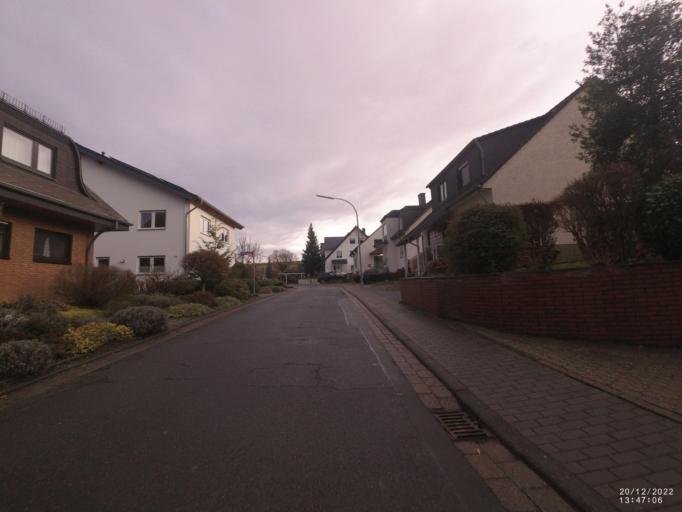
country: DE
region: Rheinland-Pfalz
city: Sinzig
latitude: 50.5362
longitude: 7.2264
